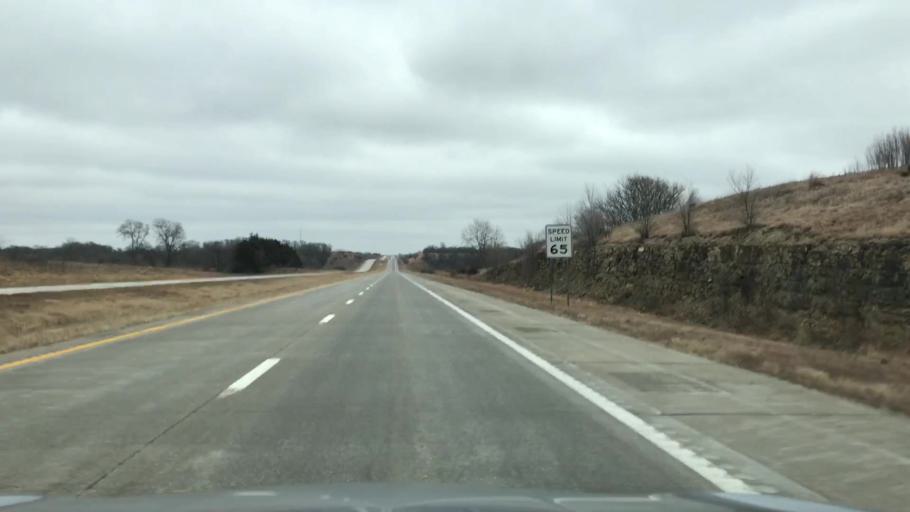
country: US
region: Missouri
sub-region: Caldwell County
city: Hamilton
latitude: 39.7350
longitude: -93.8310
